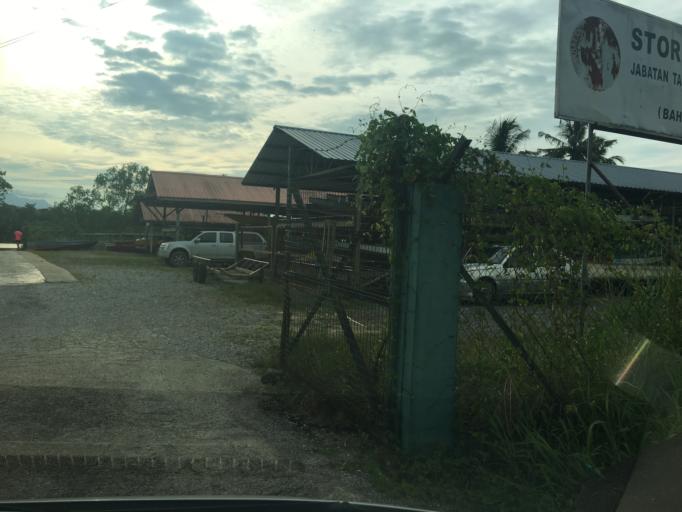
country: MY
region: Sarawak
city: Kuching
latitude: 1.5598
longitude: 110.3290
